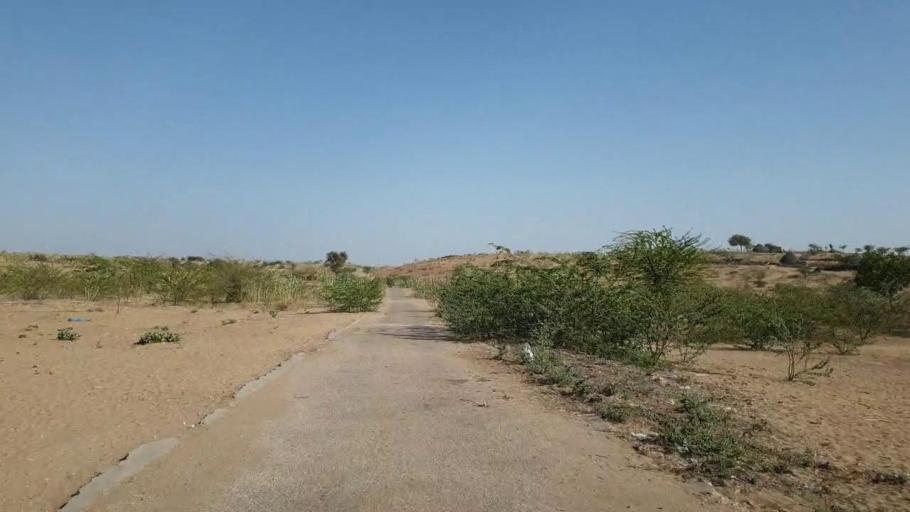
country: PK
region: Sindh
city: Islamkot
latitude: 25.0376
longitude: 70.0244
